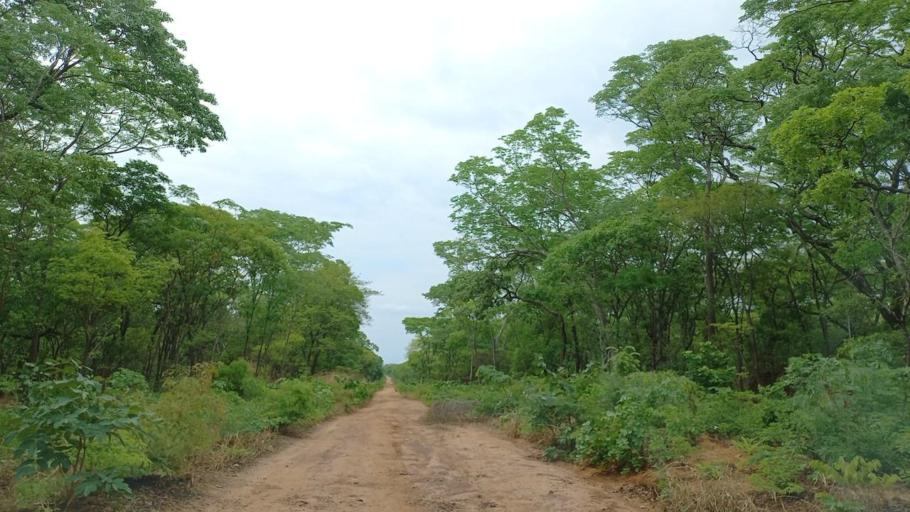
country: ZM
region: North-Western
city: Kalengwa
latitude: -13.5830
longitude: 24.9715
